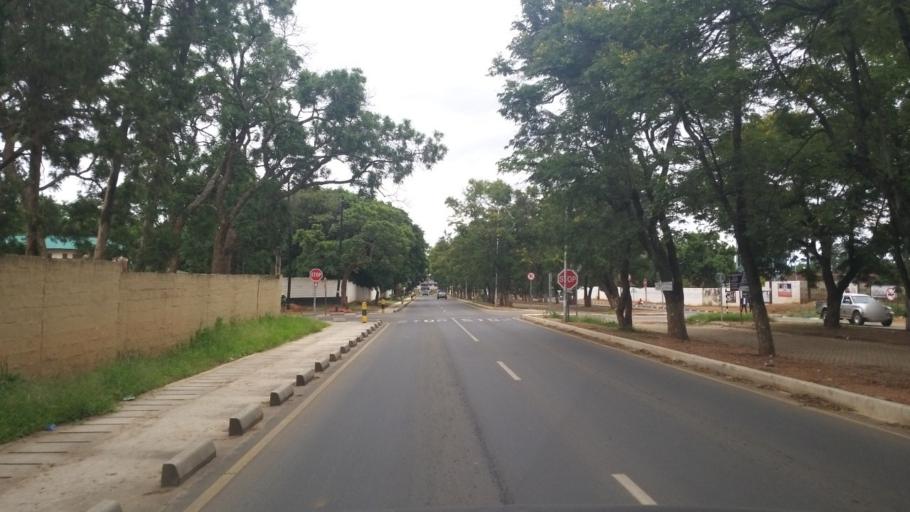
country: ZM
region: Lusaka
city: Lusaka
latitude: -15.4170
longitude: 28.3043
